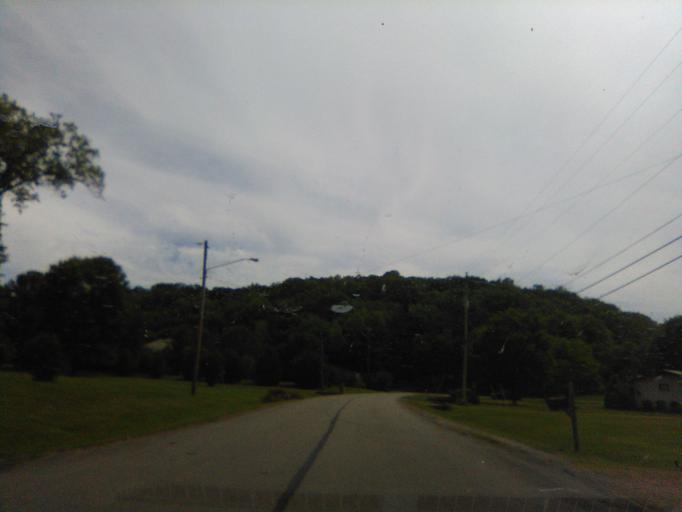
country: US
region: Tennessee
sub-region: Davidson County
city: Belle Meade
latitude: 36.1156
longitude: -86.9037
